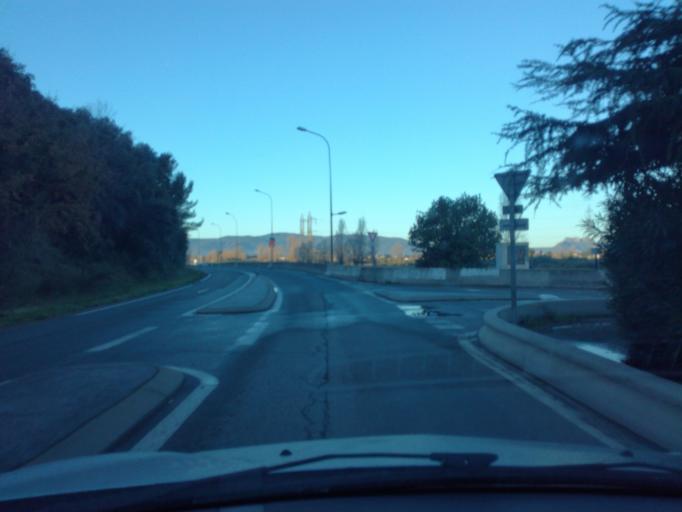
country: FR
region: Provence-Alpes-Cote d'Azur
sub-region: Departement du Var
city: Frejus
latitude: 43.4412
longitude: 6.7343
